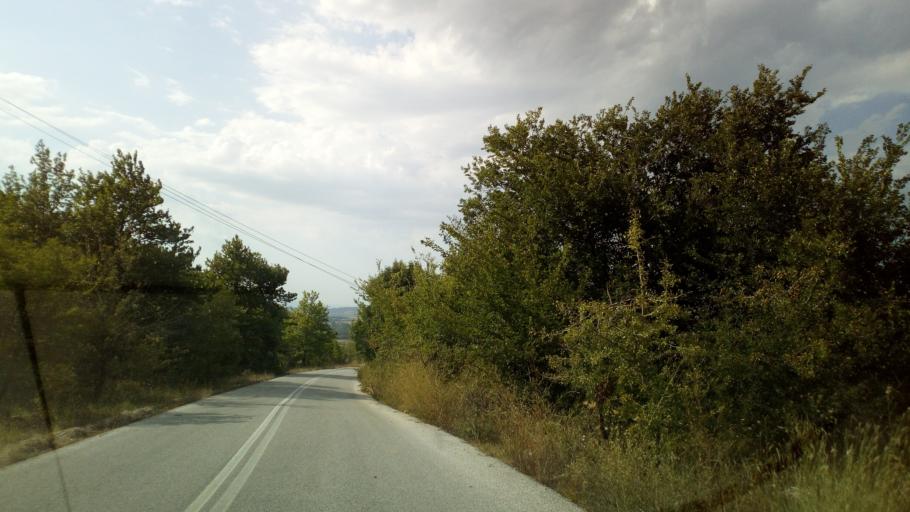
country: GR
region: Central Macedonia
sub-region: Nomos Chalkidikis
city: Galatista
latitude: 40.5433
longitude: 23.3289
